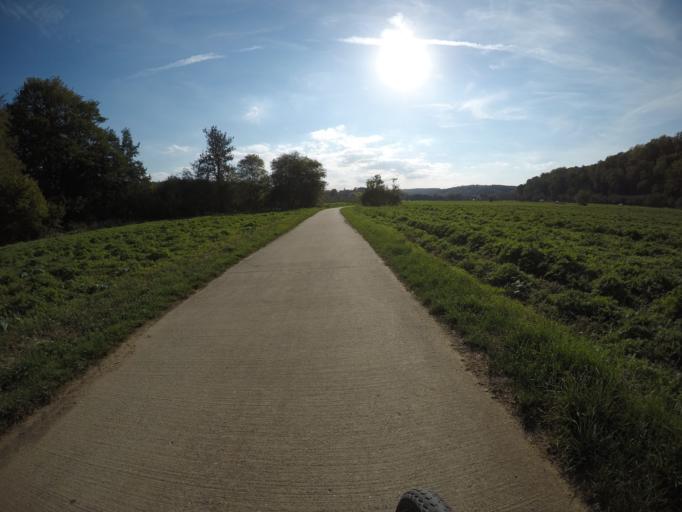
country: DE
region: Baden-Wuerttemberg
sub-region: Regierungsbezirk Stuttgart
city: Neckartailfingen
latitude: 48.6016
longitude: 9.2539
